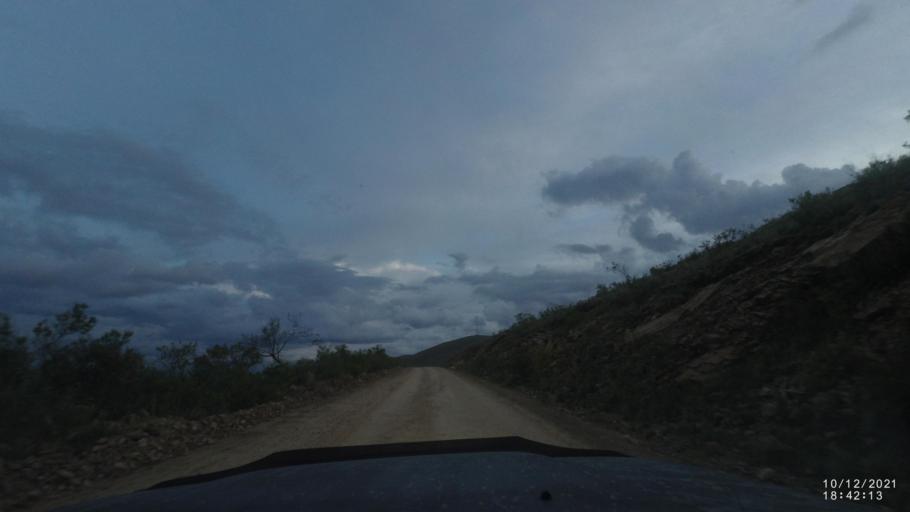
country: BO
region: Cochabamba
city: Tarata
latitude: -17.8677
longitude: -65.9850
